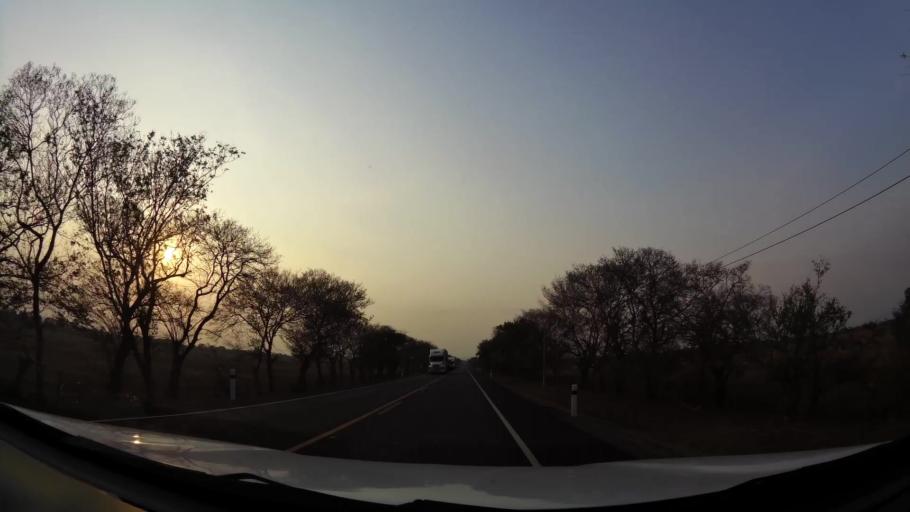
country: NI
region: Leon
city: Nagarote
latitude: 12.3022
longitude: -86.5975
